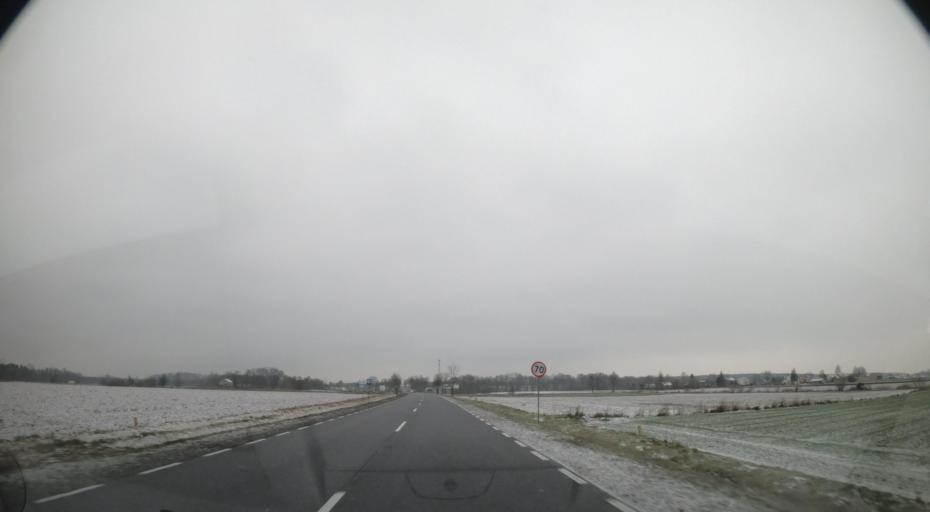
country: PL
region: Masovian Voivodeship
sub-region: Powiat plocki
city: Bodzanow
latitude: 52.4532
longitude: 19.9966
